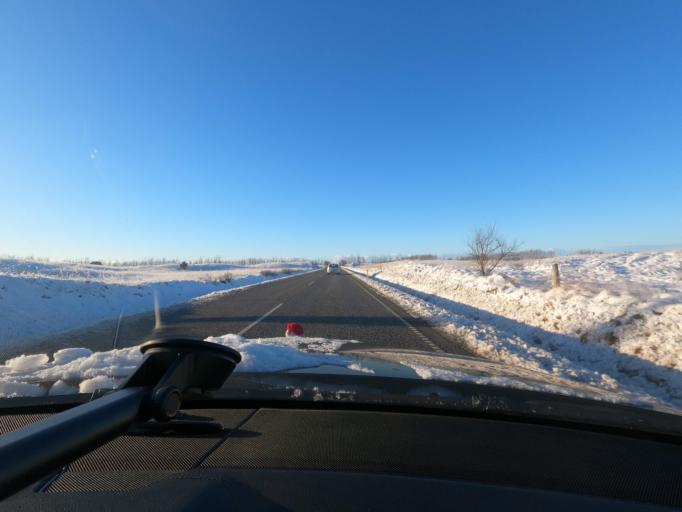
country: DK
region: South Denmark
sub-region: Tonder Kommune
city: Sherrebek
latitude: 55.1763
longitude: 8.8284
